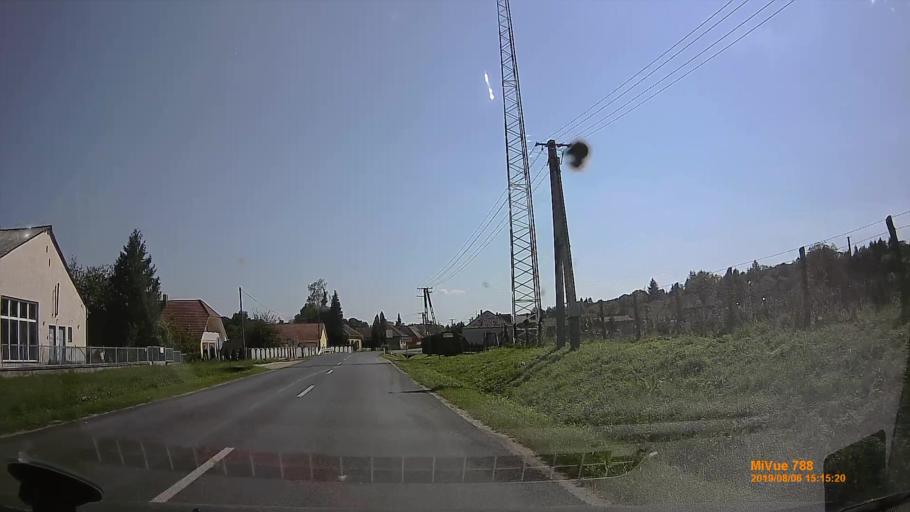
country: HU
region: Zala
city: Murakeresztur
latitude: 46.3293
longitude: 16.9712
